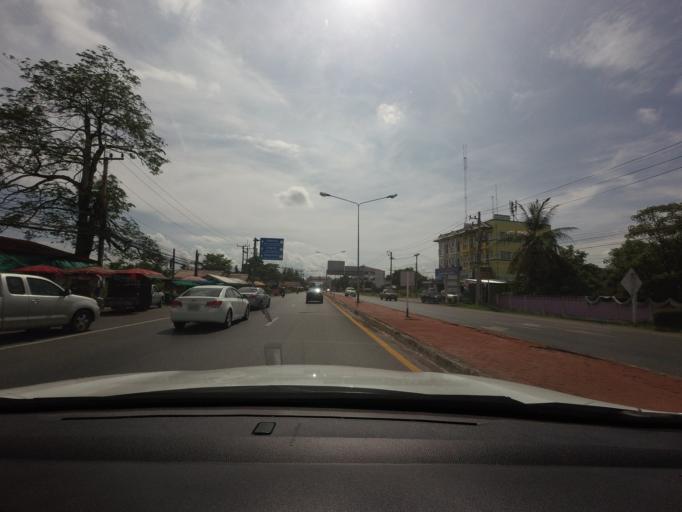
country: TH
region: Nakhon Nayok
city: Nakhon Nayok
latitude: 14.1994
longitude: 101.1942
